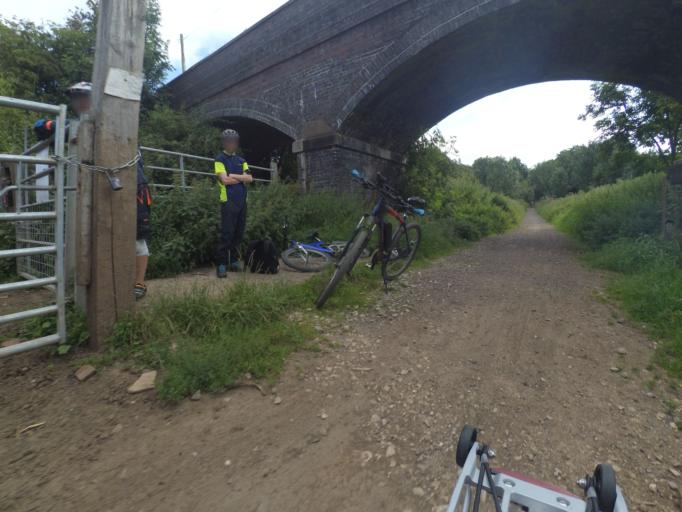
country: GB
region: England
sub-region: Staffordshire
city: Gnosall
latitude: 52.7840
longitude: -2.2261
